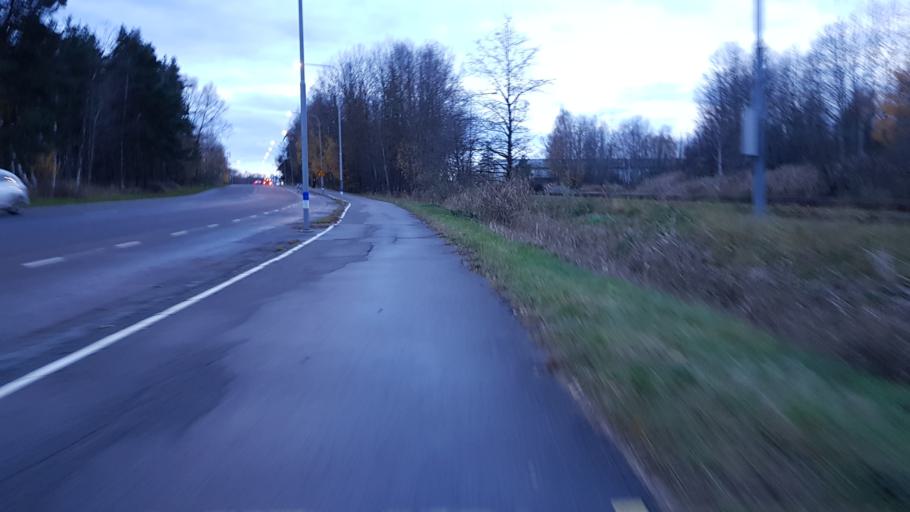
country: SE
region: OEstergoetland
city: Lindo
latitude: 58.5976
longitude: 16.2356
